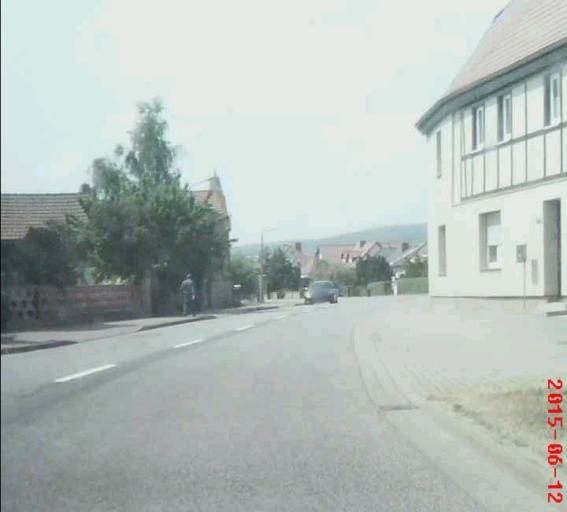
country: DE
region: Saxony-Anhalt
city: Bennungen
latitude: 51.4617
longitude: 11.1173
